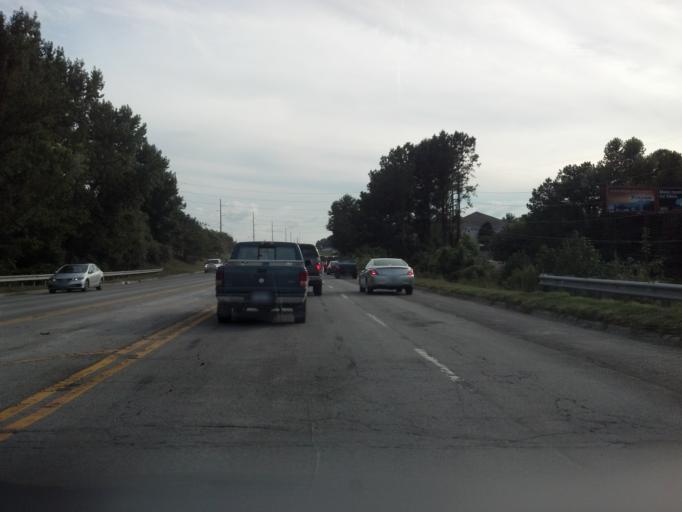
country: US
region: North Carolina
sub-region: Pitt County
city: Greenville
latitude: 35.6055
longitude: -77.3315
